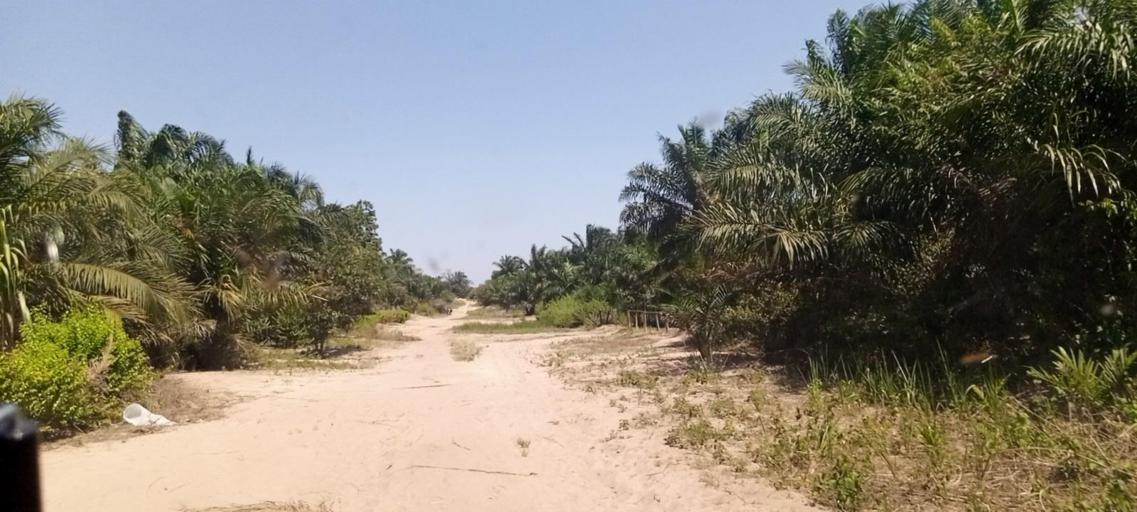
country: CD
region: Kasai-Oriental
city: Kabinda
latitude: -5.9515
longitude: 24.8044
